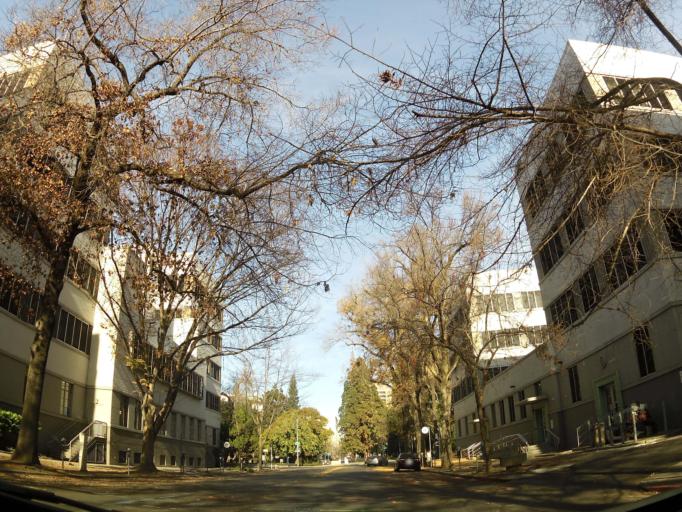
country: US
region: California
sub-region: Sacramento County
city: Sacramento
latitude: 38.5745
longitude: -121.4930
